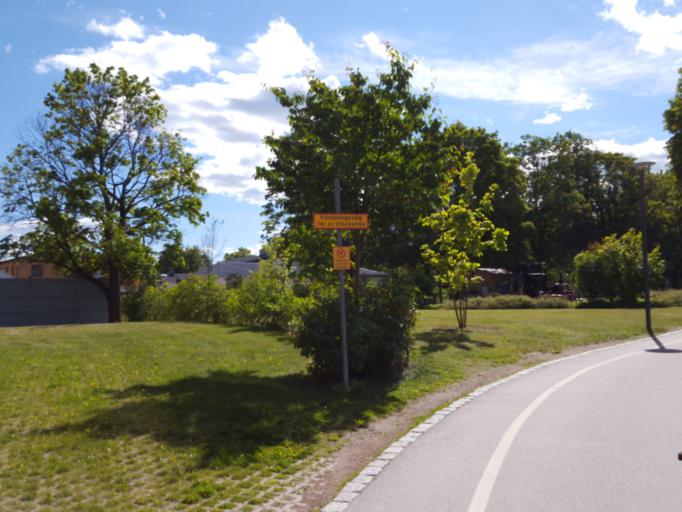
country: SE
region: Uppsala
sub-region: Uppsala Kommun
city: Uppsala
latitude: 59.8576
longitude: 17.6583
